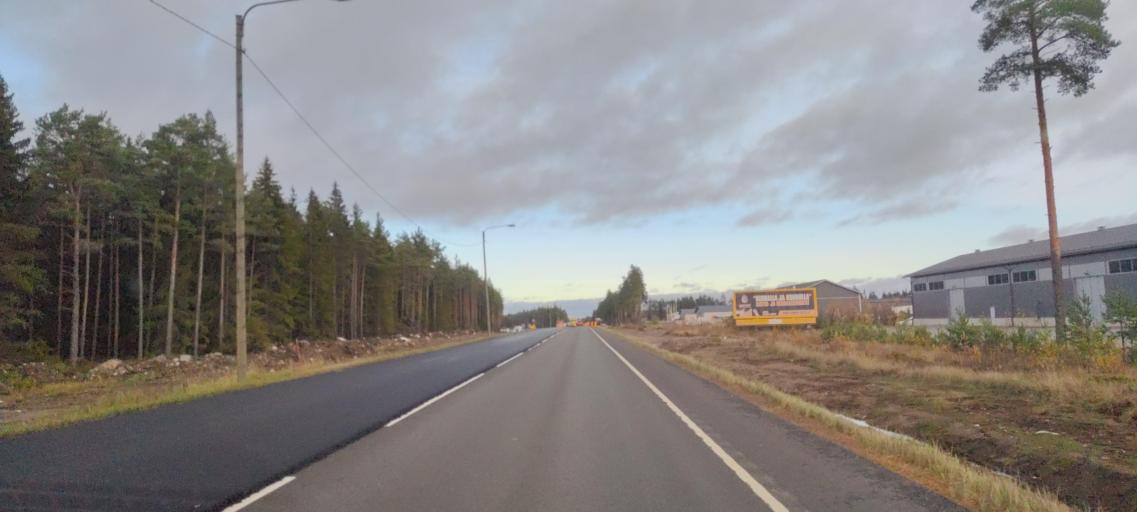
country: FI
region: Satakunta
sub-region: Rauma
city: Eurajoki
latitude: 61.1911
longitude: 21.6948
